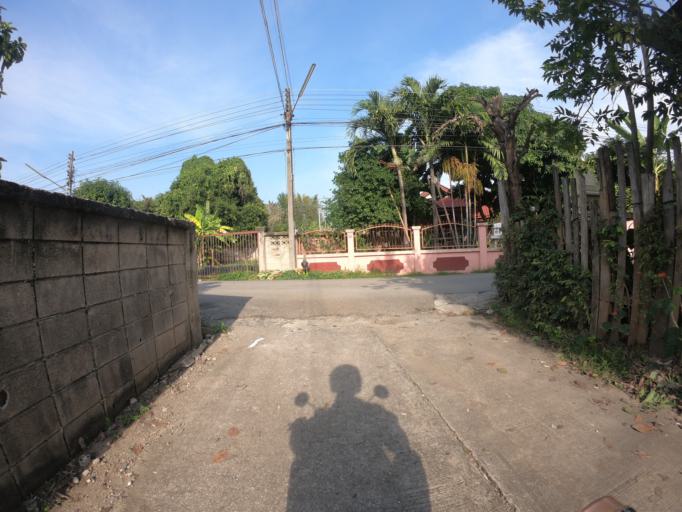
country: TH
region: Chiang Mai
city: Chiang Mai
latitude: 18.8347
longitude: 98.9941
